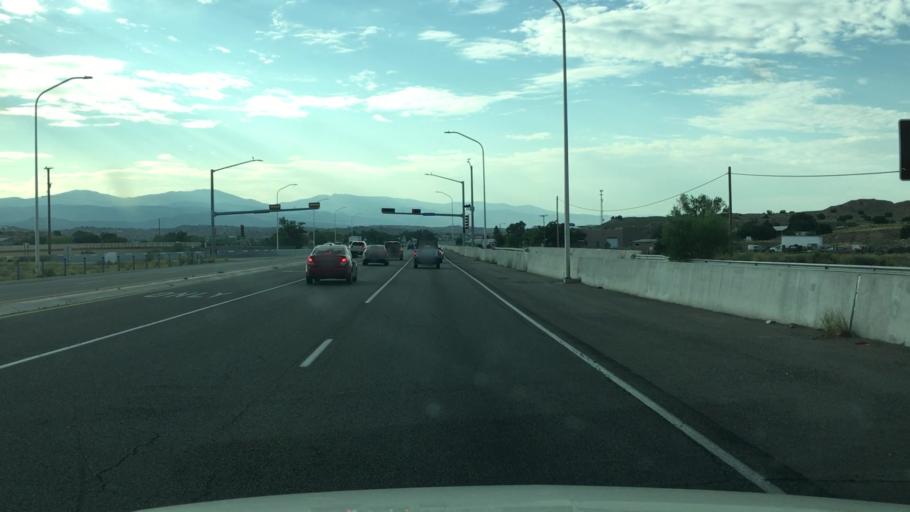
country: US
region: New Mexico
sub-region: Santa Fe County
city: El Valle de Arroyo Seco
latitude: 35.9628
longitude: -106.0298
